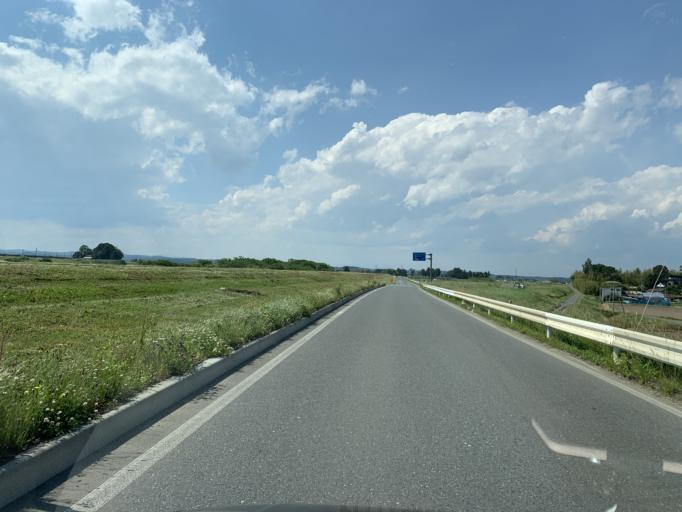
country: JP
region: Miyagi
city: Matsushima
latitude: 38.4376
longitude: 141.1181
